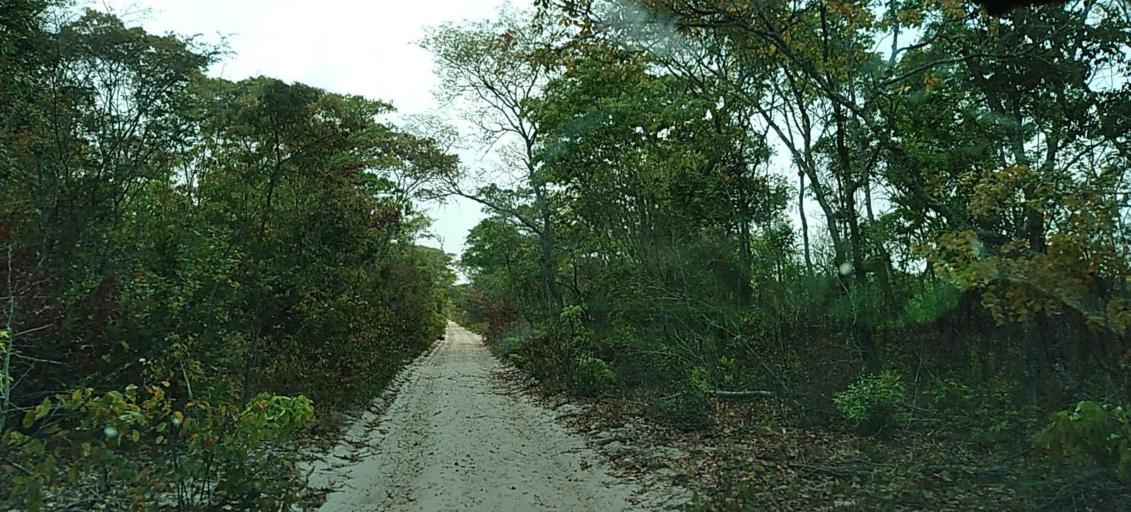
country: ZM
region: North-Western
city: Kabompo
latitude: -13.3979
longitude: 23.8042
